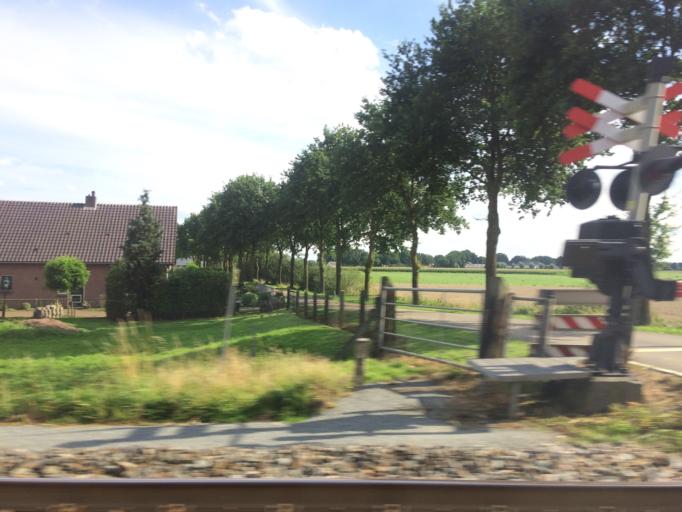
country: NL
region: Gelderland
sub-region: Gemeente Wijchen
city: Wijchen
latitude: 51.8064
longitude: 5.6807
